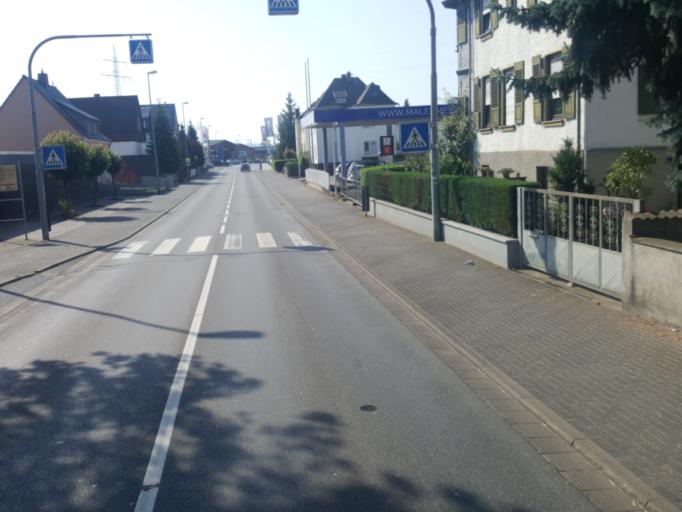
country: DE
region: Hesse
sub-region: Regierungsbezirk Giessen
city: Elz
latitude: 50.4064
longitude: 8.0369
